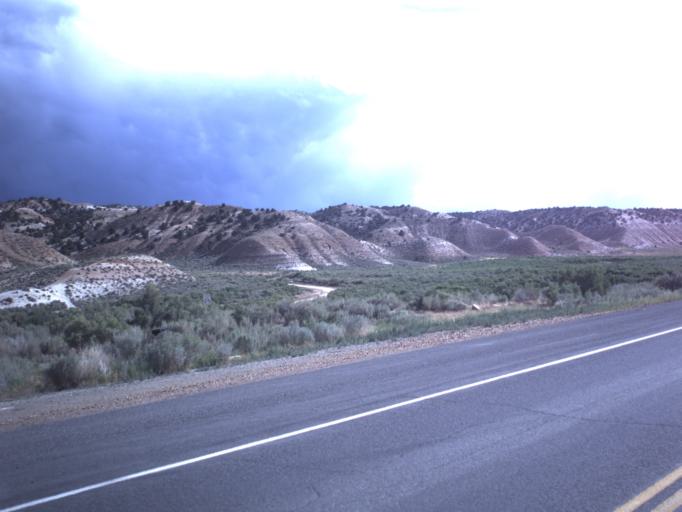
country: US
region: Utah
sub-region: Duchesne County
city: Duchesne
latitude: 40.1366
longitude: -110.4261
